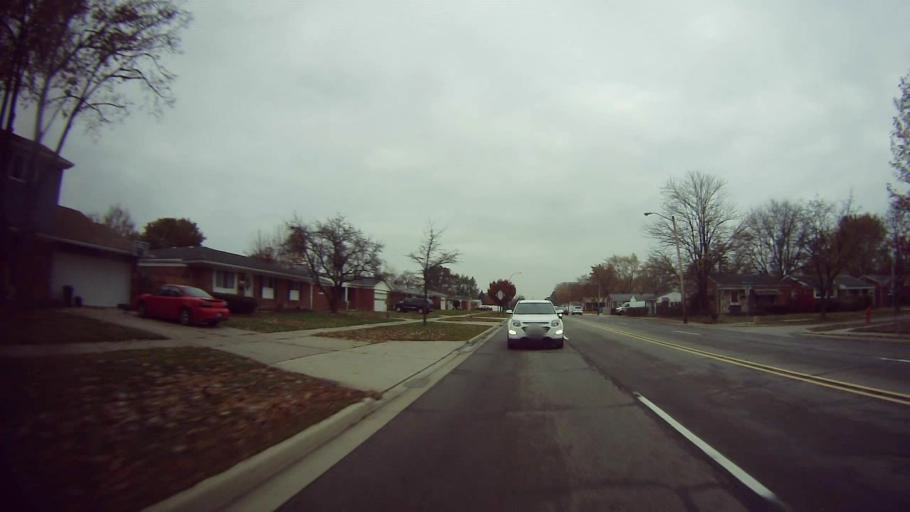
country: US
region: Michigan
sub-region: Oakland County
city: Clawson
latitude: 42.5273
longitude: -83.1259
